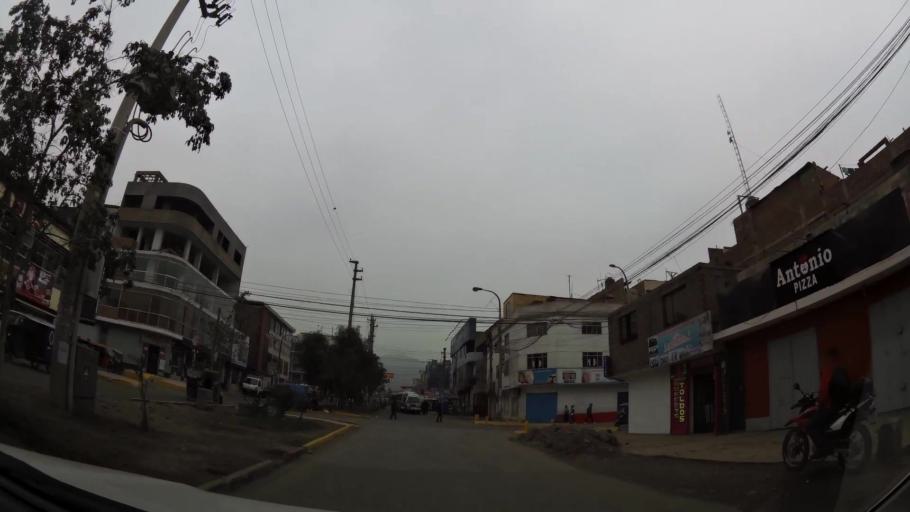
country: PE
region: Lima
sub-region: Lima
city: Independencia
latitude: -11.9471
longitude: -76.9858
